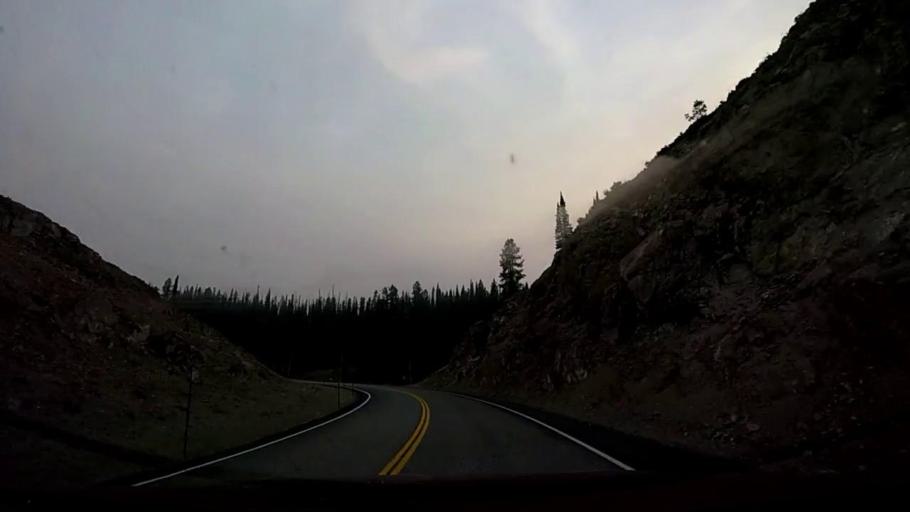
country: US
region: Idaho
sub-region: Blaine County
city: Ketchum
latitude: 43.8822
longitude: -114.7012
